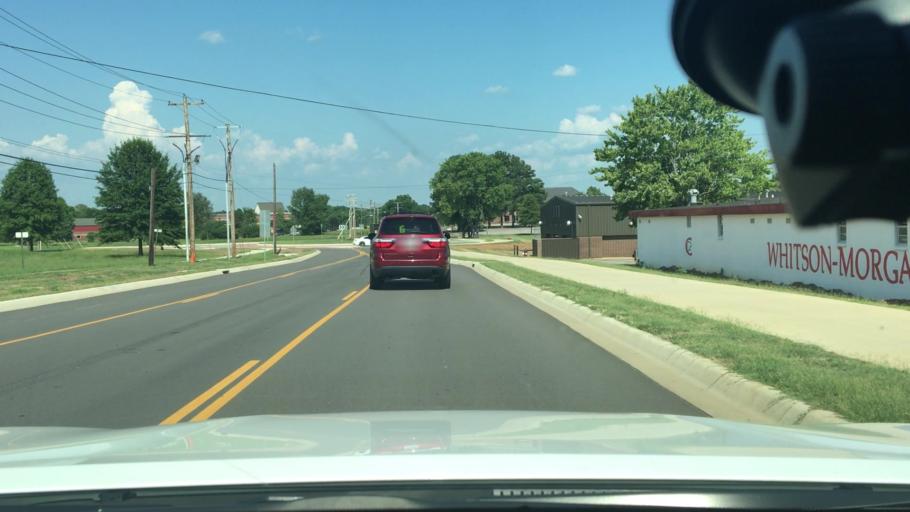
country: US
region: Arkansas
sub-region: Johnson County
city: Clarksville
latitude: 35.4617
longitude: -93.4868
